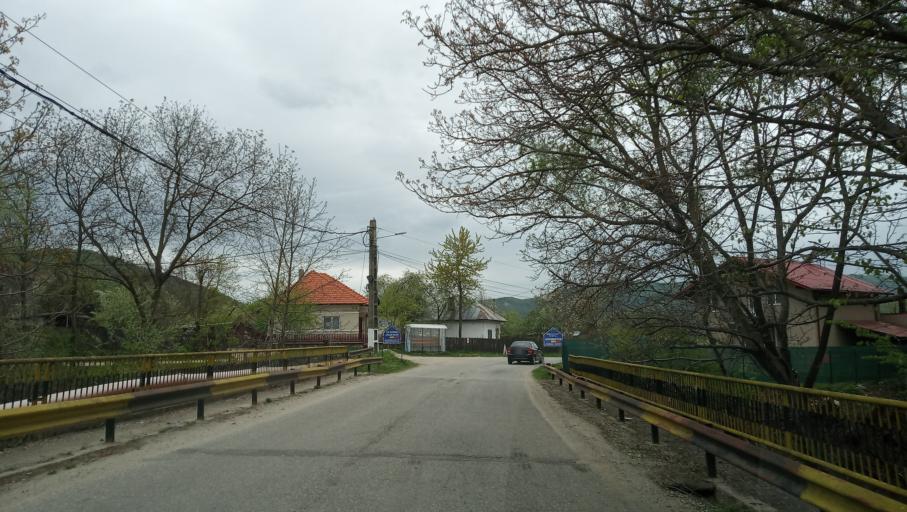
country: RO
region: Valcea
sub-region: Comuna Daesti
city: Daesti
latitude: 45.1839
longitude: 24.3844
